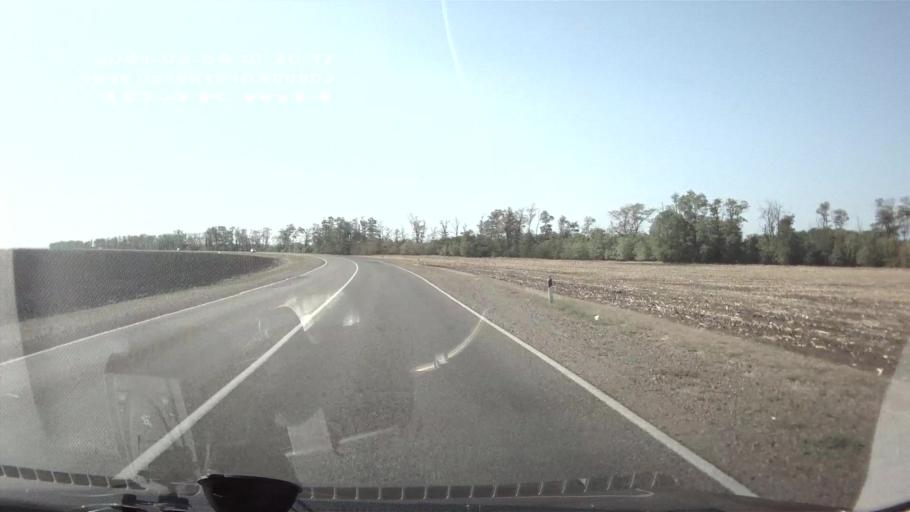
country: RU
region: Krasnodarskiy
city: Belaya Glina
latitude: 46.0532
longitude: 40.8004
